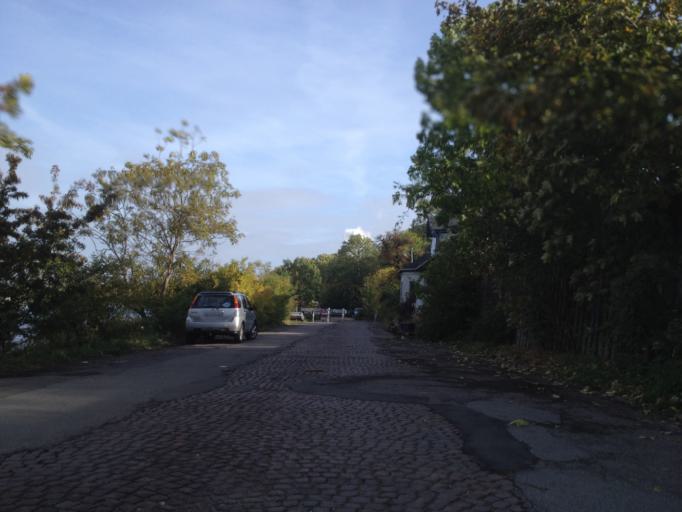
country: DK
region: Capital Region
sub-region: Kobenhavn
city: Christianshavn
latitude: 55.6763
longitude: 12.6068
